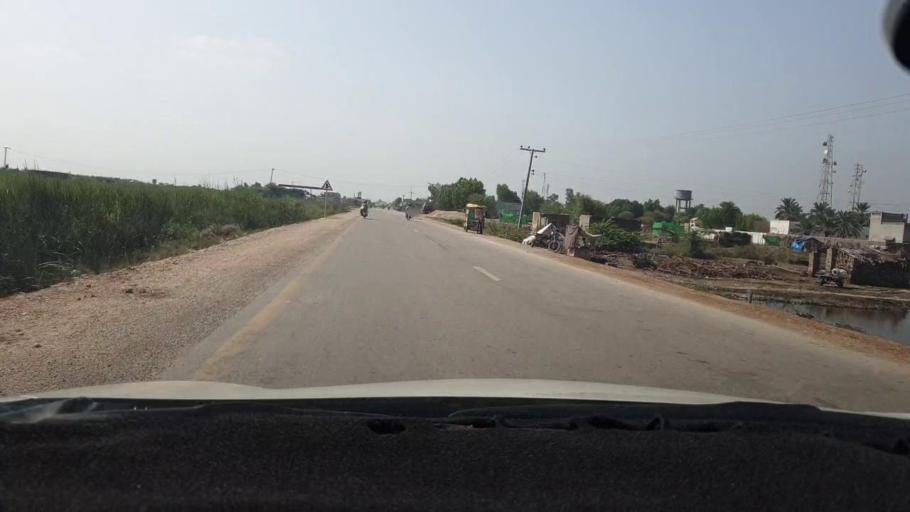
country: PK
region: Sindh
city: Tando Mittha Khan
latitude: 25.8035
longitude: 69.0722
